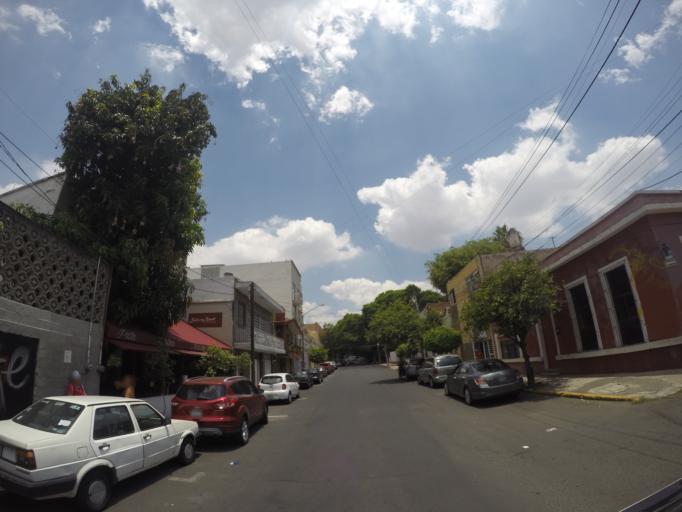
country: MX
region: Jalisco
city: Guadalajara
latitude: 20.6762
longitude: -103.3630
